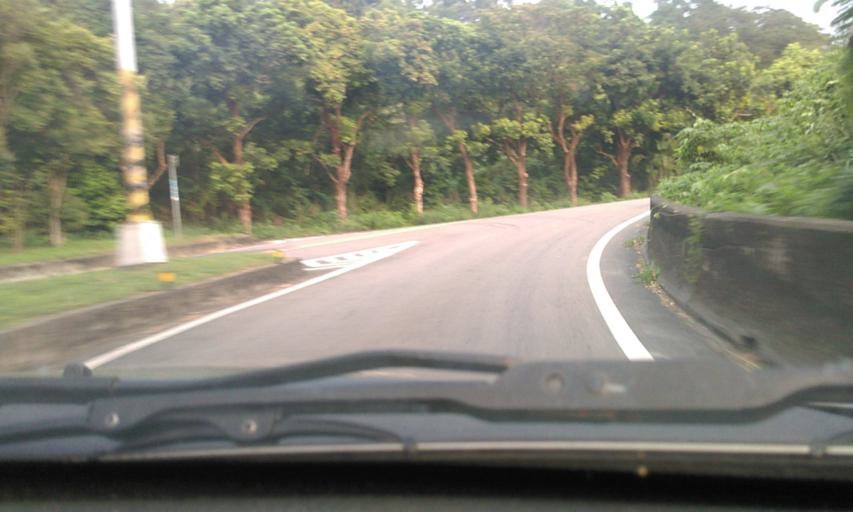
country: TW
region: Taiwan
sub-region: Hsinchu
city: Hsinchu
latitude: 24.6888
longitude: 120.9758
